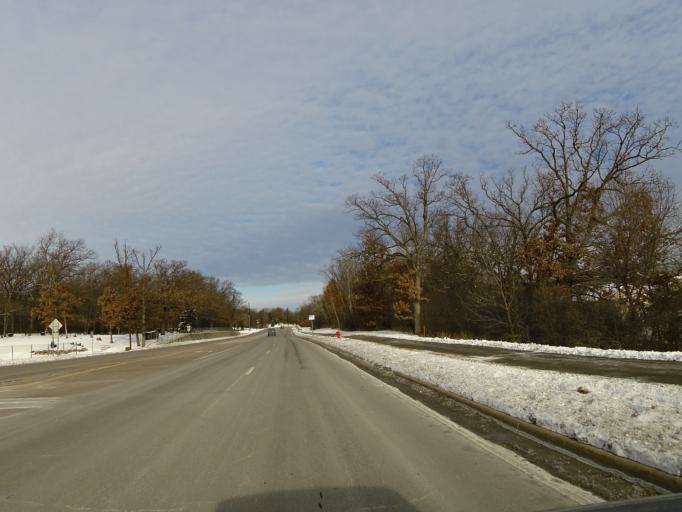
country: US
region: Minnesota
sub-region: Dakota County
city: Burnsville
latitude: 44.7154
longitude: -93.2971
